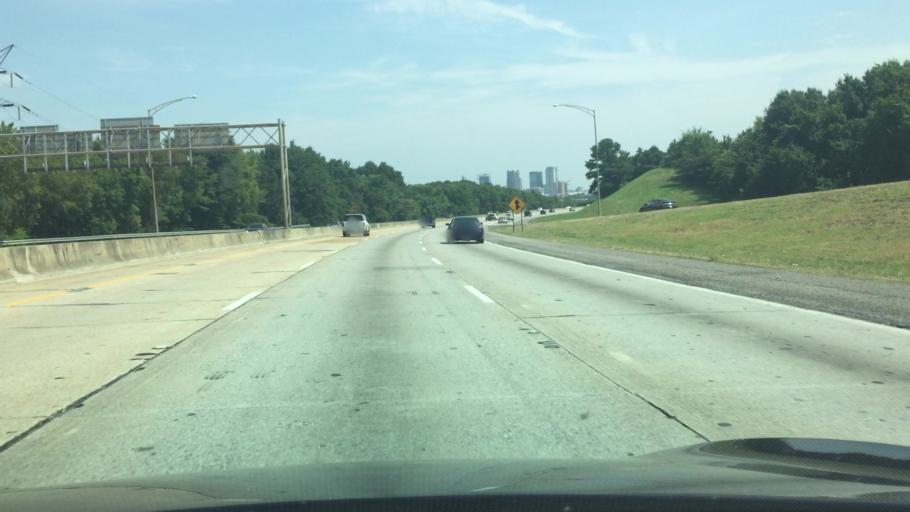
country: US
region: Alabama
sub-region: Jefferson County
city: Homewood
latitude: 33.4855
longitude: -86.8257
